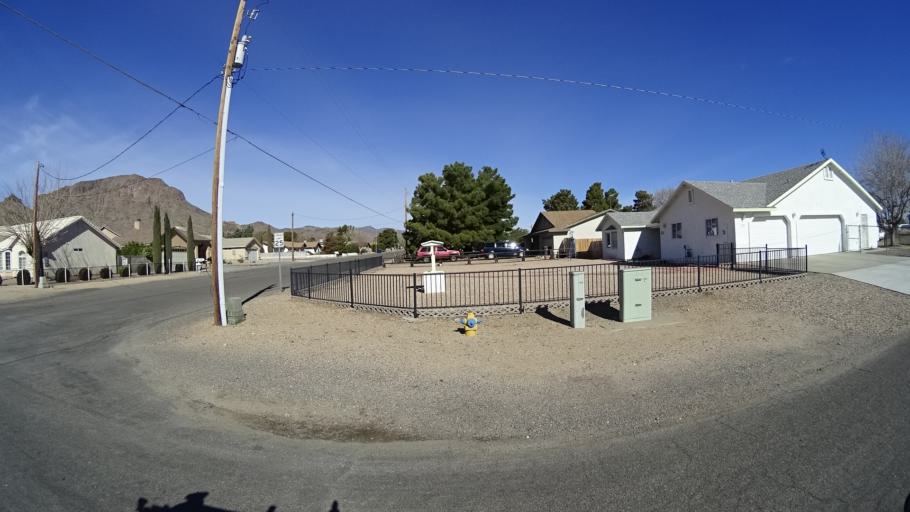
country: US
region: Arizona
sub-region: Mohave County
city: New Kingman-Butler
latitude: 35.2627
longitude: -114.0414
